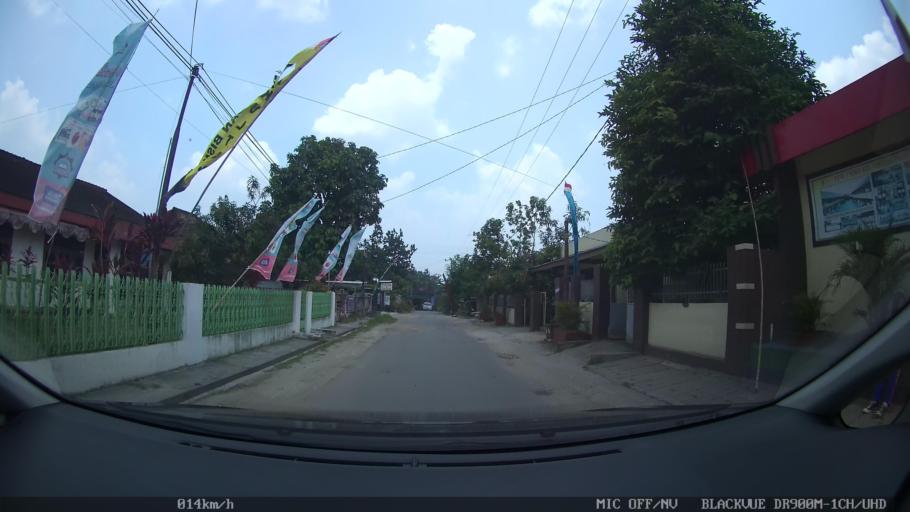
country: ID
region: Lampung
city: Pringsewu
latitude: -5.3475
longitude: 104.9742
